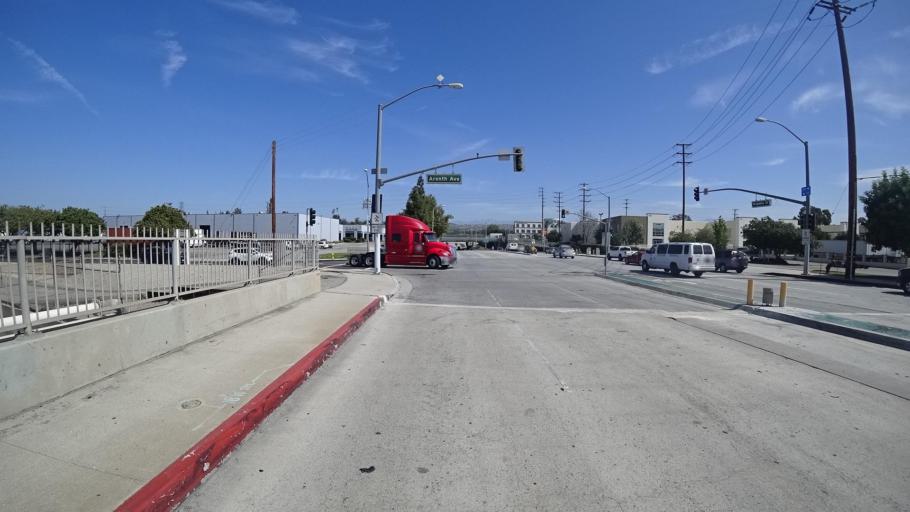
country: US
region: California
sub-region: Los Angeles County
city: South San Jose Hills
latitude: 34.0010
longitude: -117.8880
